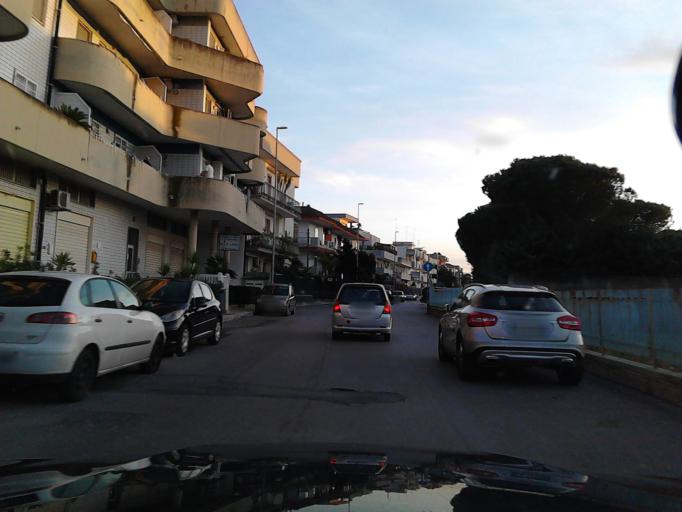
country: IT
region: Apulia
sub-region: Provincia di Bari
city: Capurso
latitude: 41.0509
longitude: 16.9155
